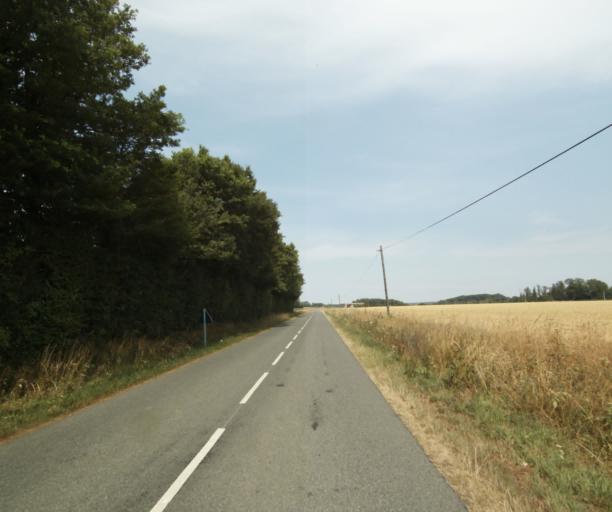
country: FR
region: Centre
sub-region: Departement d'Eure-et-Loir
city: La Bazoche-Gouet
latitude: 48.1785
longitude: 0.9495
